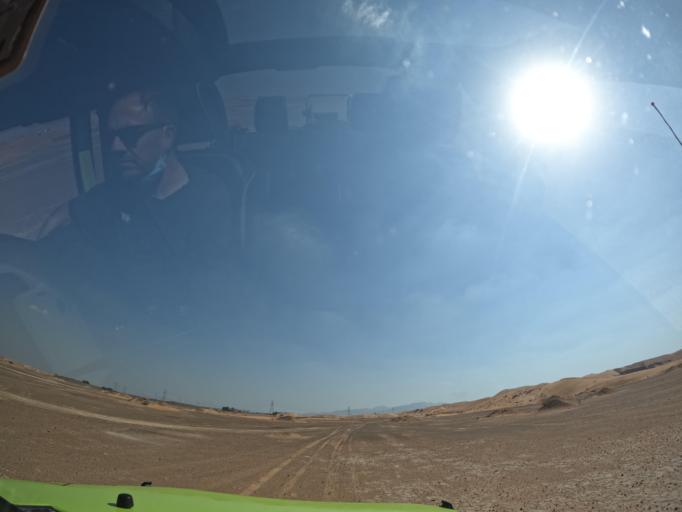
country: AE
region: Ash Shariqah
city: Adh Dhayd
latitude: 24.7965
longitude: 55.7854
